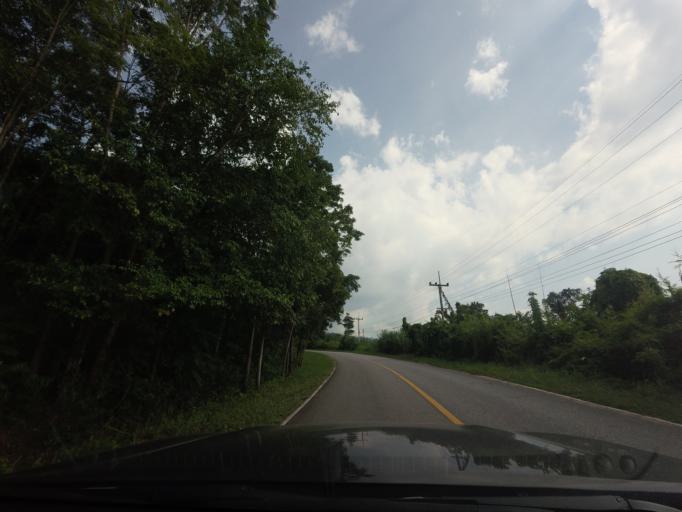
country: TH
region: Phitsanulok
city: Nakhon Thai
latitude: 17.0196
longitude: 100.9446
